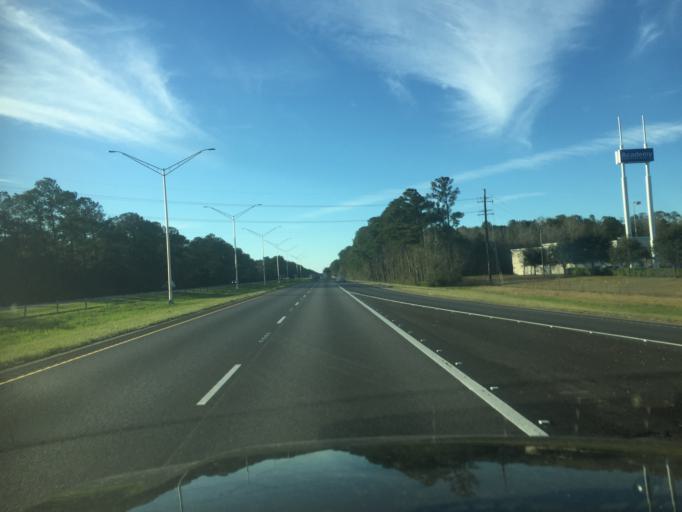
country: US
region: Louisiana
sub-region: Saint Tammany Parish
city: Slidell
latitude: 30.3149
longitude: -89.8302
